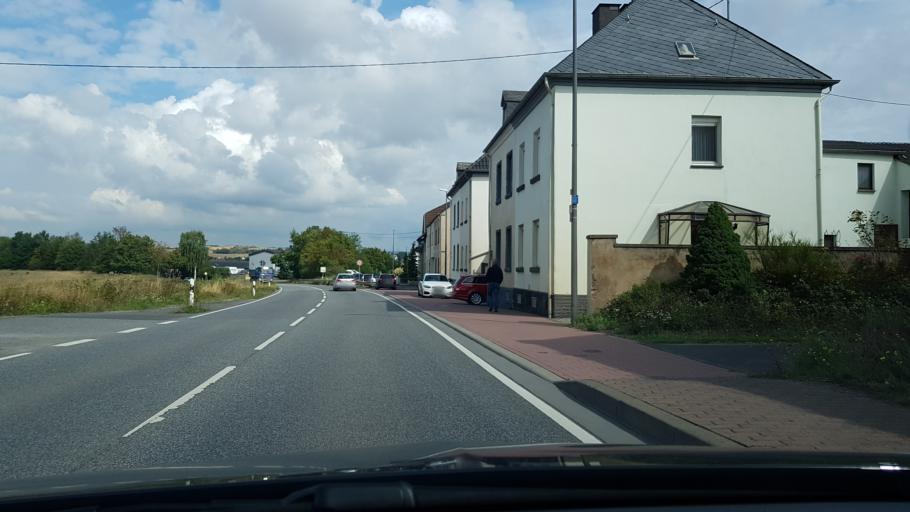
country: DE
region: Rheinland-Pfalz
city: Plaidt
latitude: 50.3833
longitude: 7.3874
